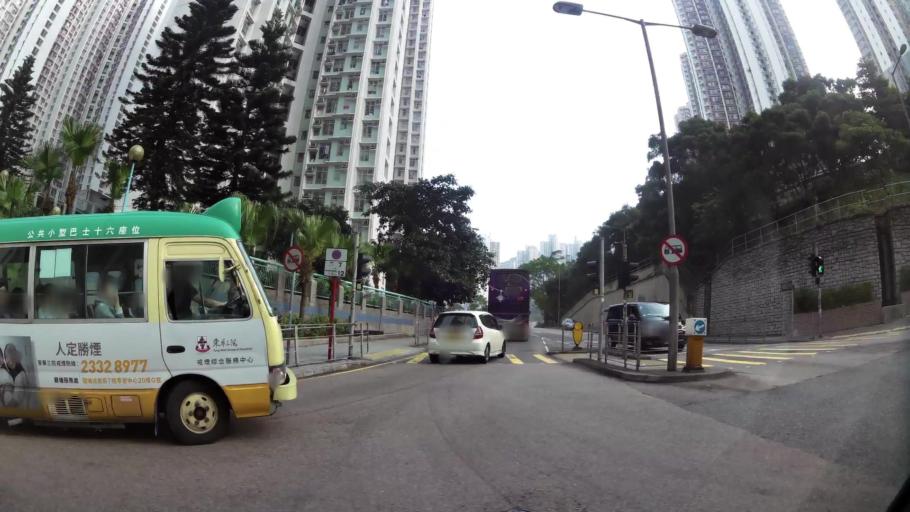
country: HK
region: Kowloon City
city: Kowloon
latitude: 22.3098
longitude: 114.2349
